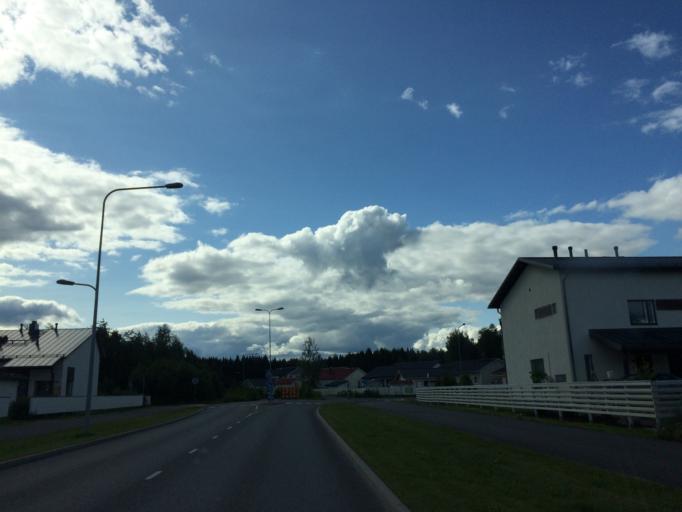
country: FI
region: Haeme
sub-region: Haemeenlinna
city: Parola
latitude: 60.9775
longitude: 24.3727
